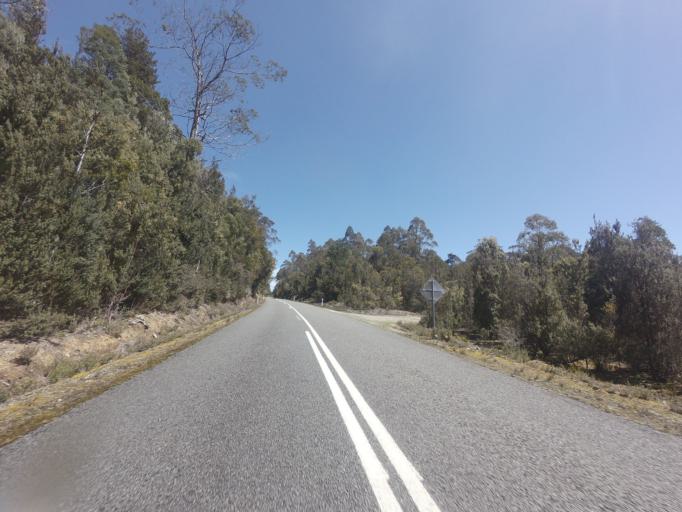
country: AU
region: Tasmania
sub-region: Huon Valley
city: Geeveston
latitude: -42.8166
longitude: 146.3646
